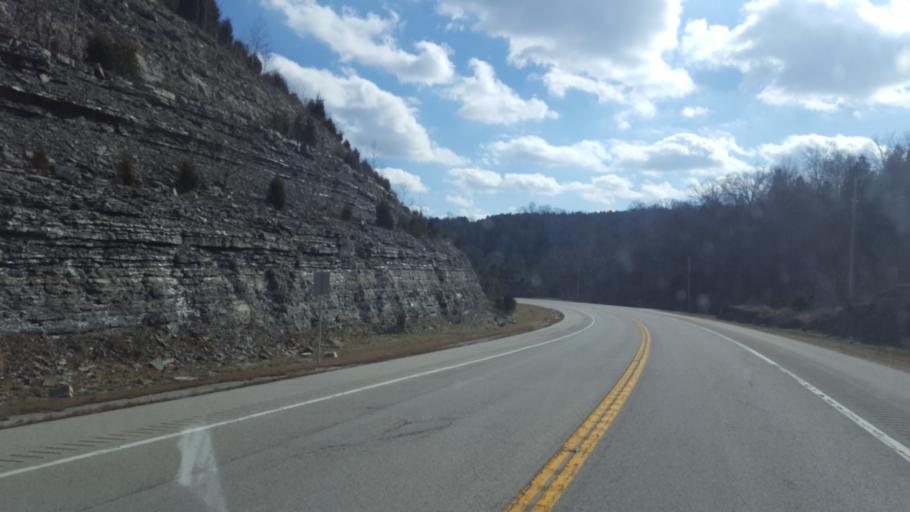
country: US
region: Kentucky
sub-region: Franklin County
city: Frankfort
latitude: 38.3466
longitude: -84.8583
